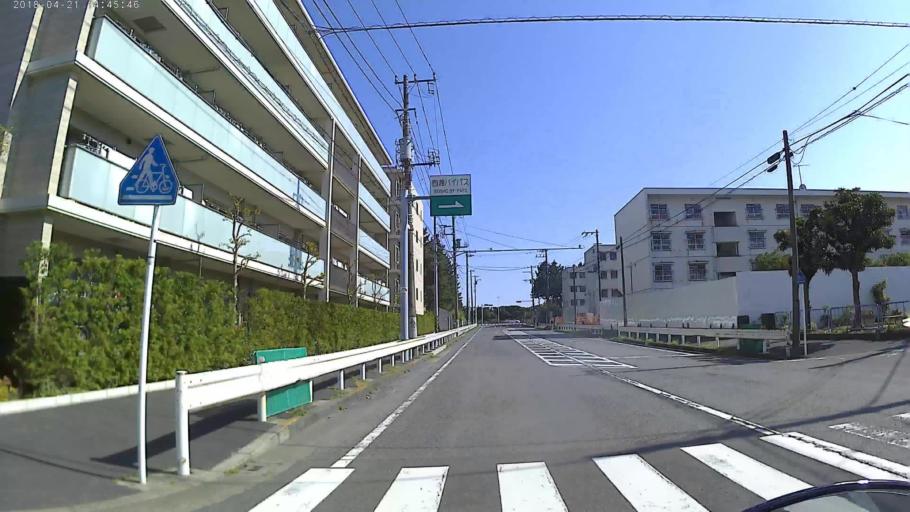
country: JP
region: Kanagawa
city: Hiratsuka
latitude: 35.3172
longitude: 139.3478
